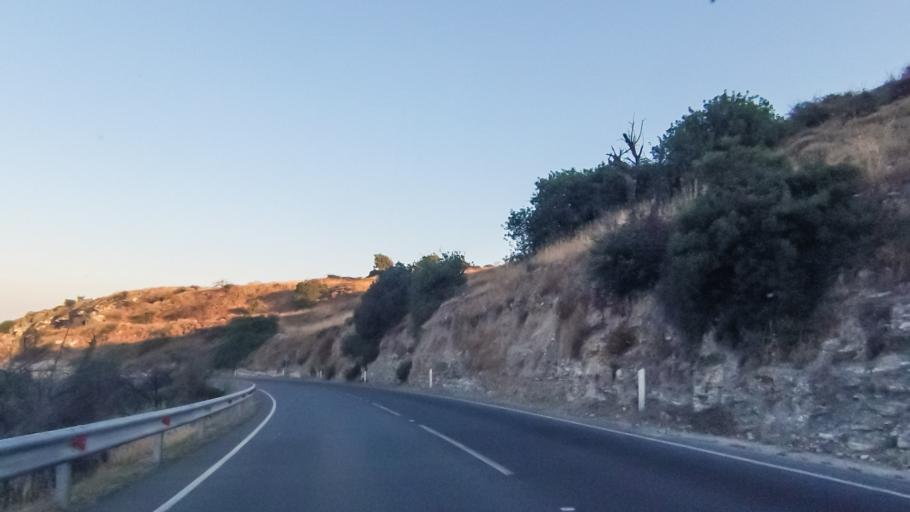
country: CY
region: Limassol
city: Erimi
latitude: 34.6672
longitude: 32.8855
